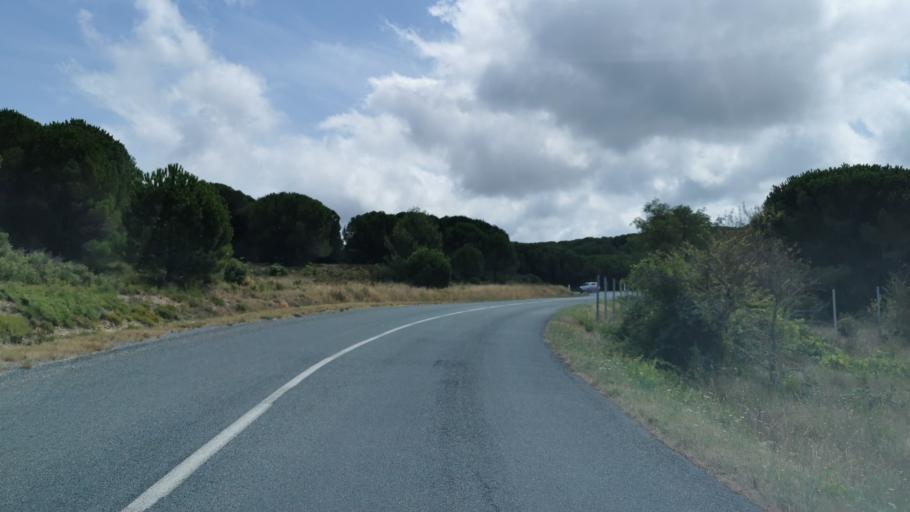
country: FR
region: Languedoc-Roussillon
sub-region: Departement de l'Aude
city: Bizanet
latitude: 43.1626
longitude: 2.8938
